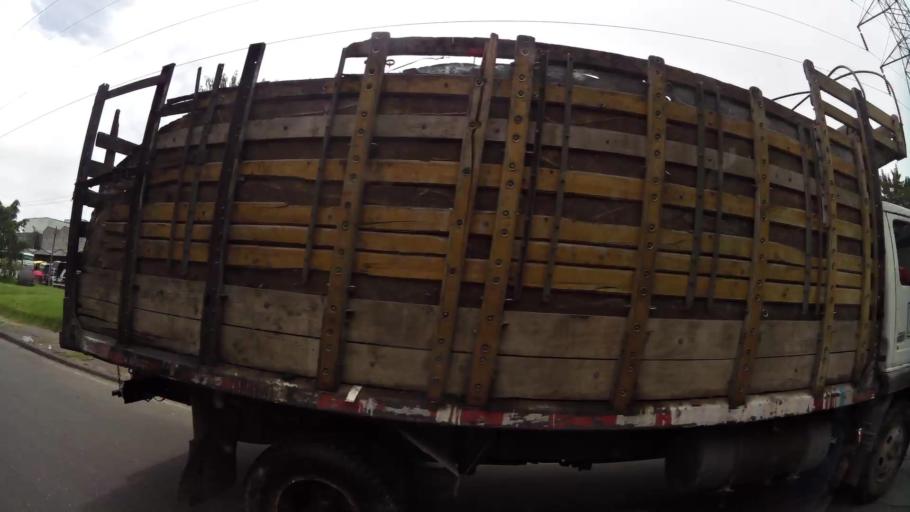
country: CO
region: Bogota D.C.
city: Bogota
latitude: 4.6424
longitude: -74.1201
